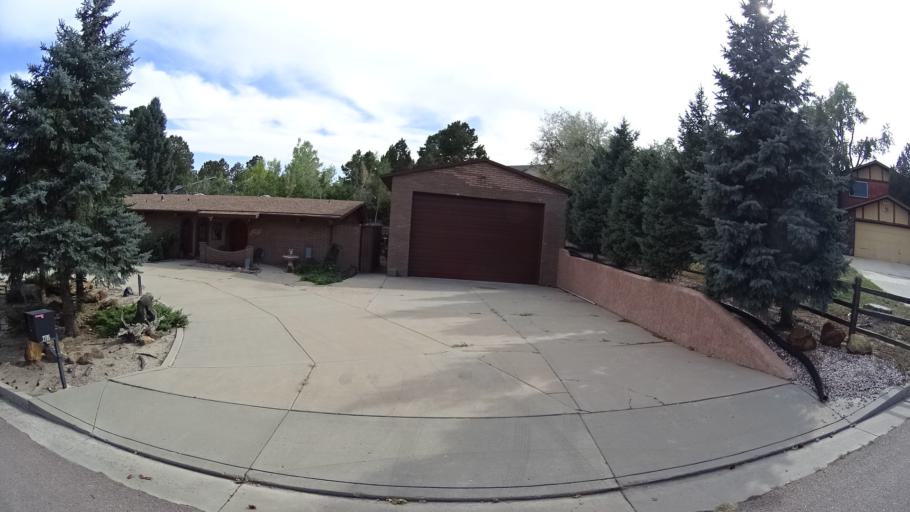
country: US
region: Colorado
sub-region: El Paso County
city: Colorado Springs
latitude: 38.8958
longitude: -104.7759
